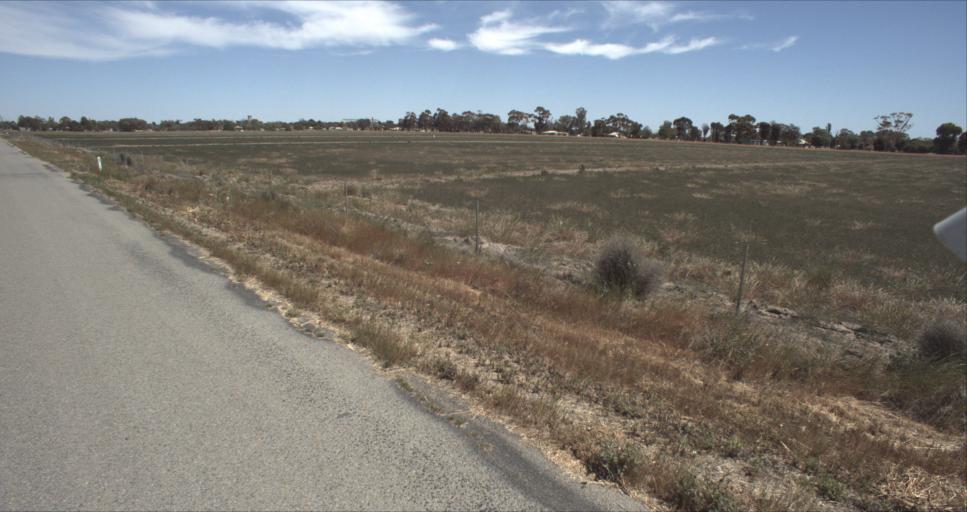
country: AU
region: New South Wales
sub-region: Leeton
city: Leeton
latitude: -34.5942
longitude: 146.4169
